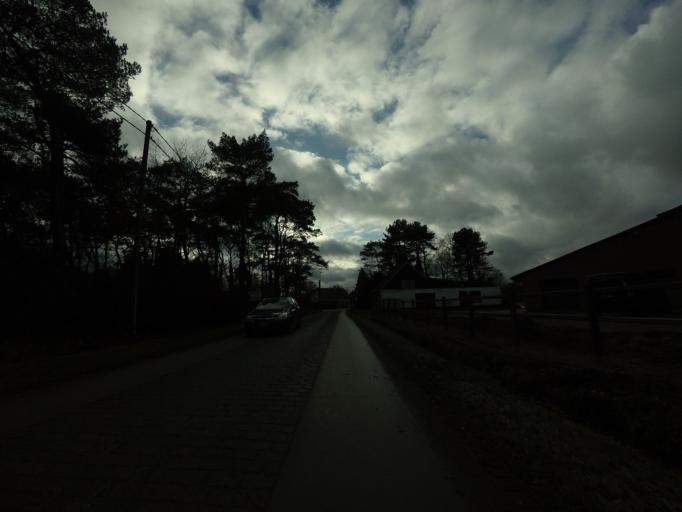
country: BE
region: Flanders
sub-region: Provincie Antwerpen
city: Stabroek
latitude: 51.3692
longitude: 4.3312
